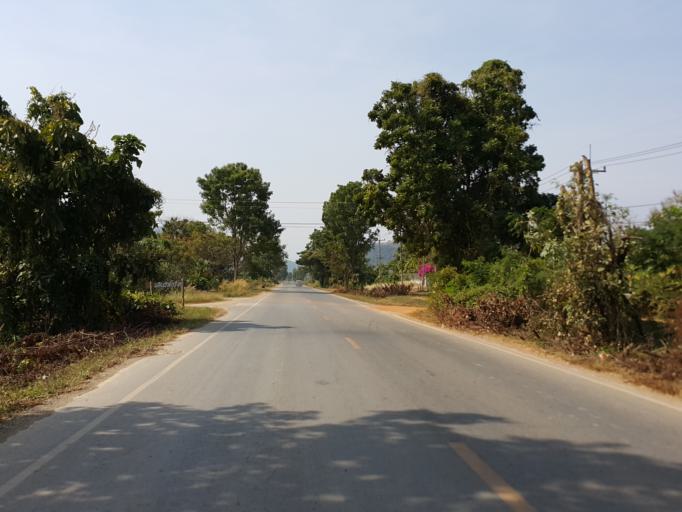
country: TH
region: Sukhothai
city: Thung Saliam
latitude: 17.3315
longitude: 99.5296
